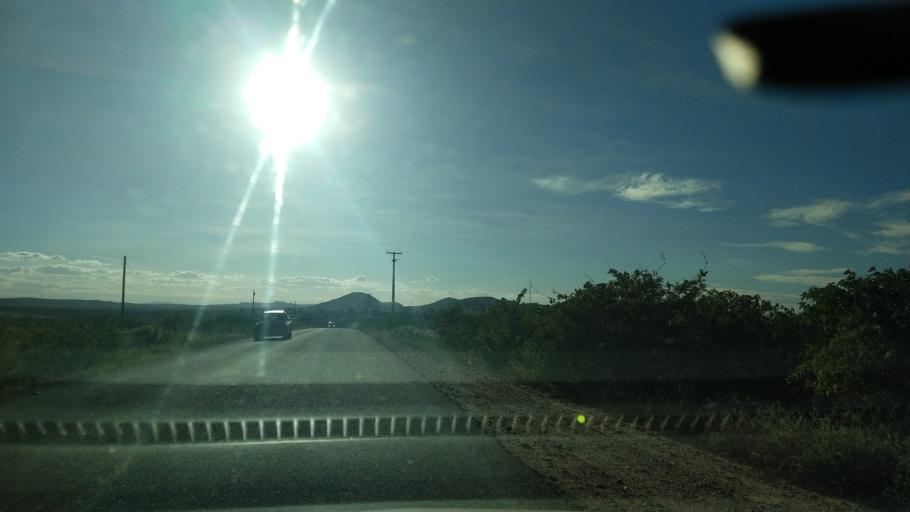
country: BR
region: Rio Grande do Norte
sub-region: Tangara
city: Tangara
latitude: -6.2100
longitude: -35.7903
